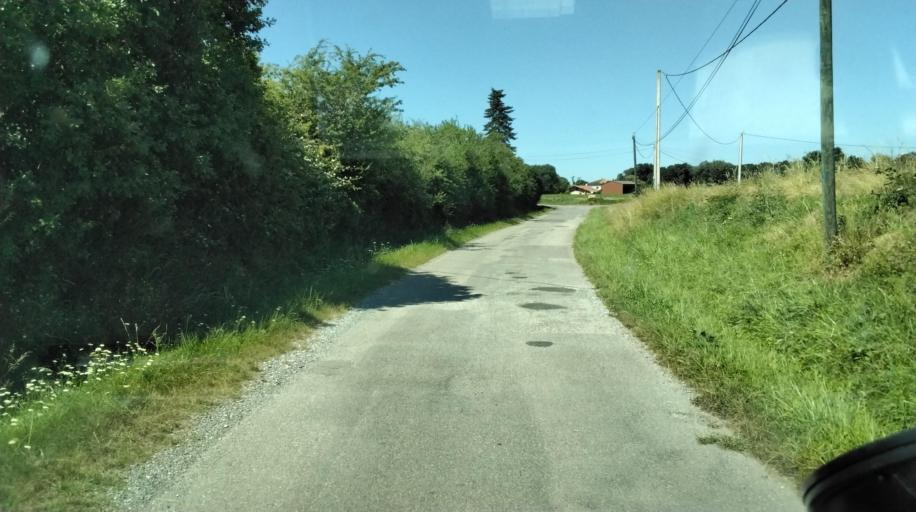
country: FR
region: Midi-Pyrenees
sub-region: Departement de la Haute-Garonne
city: Sainte-Foy-de-Peyrolieres
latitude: 43.4854
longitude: 1.1336
